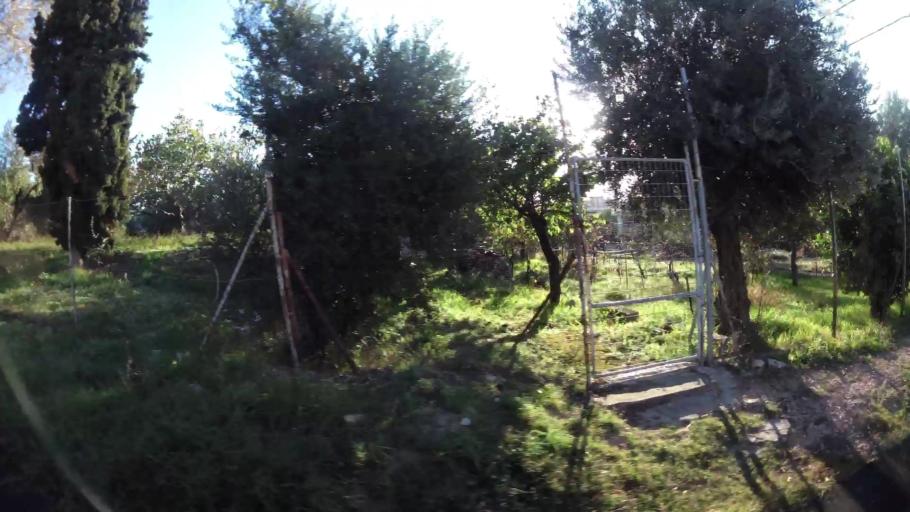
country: GR
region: Attica
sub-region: Nomarchia Anatolikis Attikis
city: Pallini
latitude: 38.0075
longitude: 23.8837
